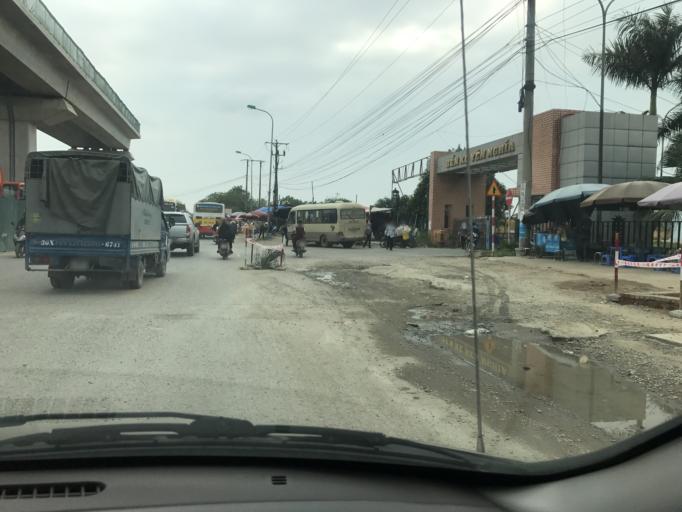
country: VN
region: Ha Noi
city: Ha Dong
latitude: 20.9489
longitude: 105.7469
